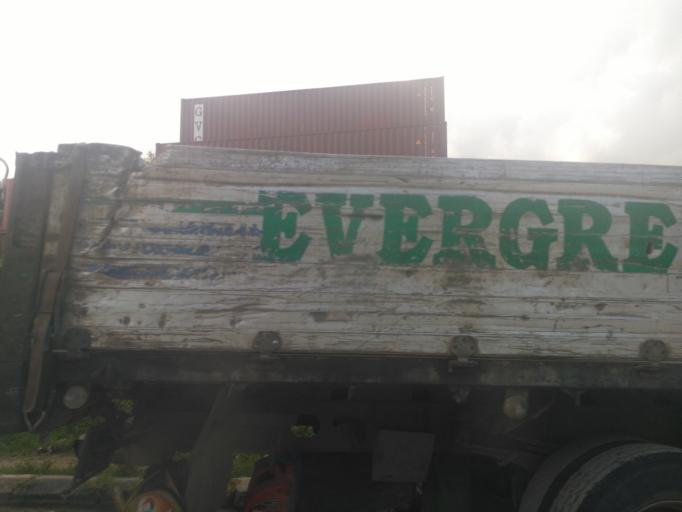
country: TZ
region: Zanzibar Urban/West
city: Zanzibar
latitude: -6.1569
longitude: 39.1964
